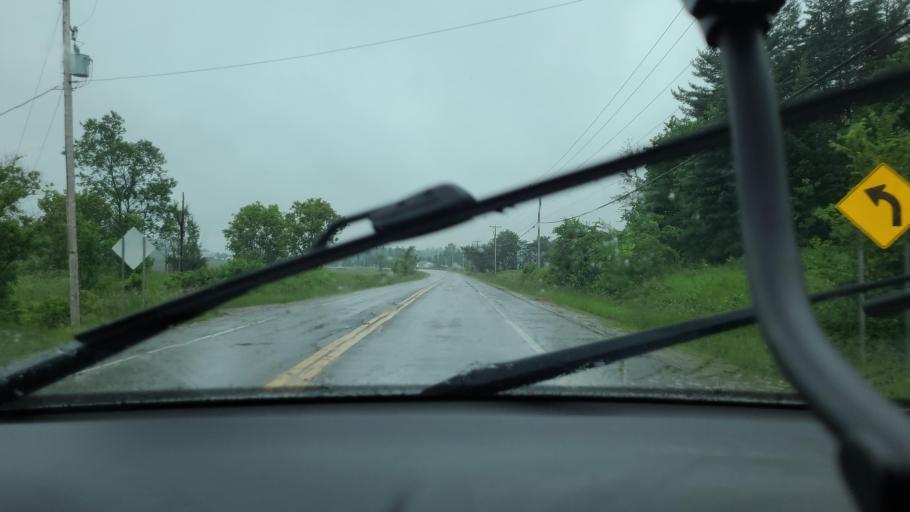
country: CA
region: Quebec
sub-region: Outaouais
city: Saint-Andre-Avellin
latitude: 45.7017
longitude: -75.0516
